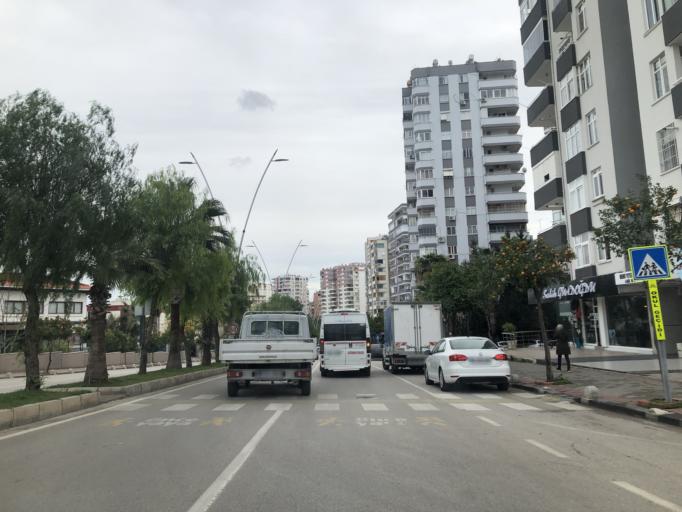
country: TR
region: Adana
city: Adana
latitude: 37.0539
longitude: 35.2892
